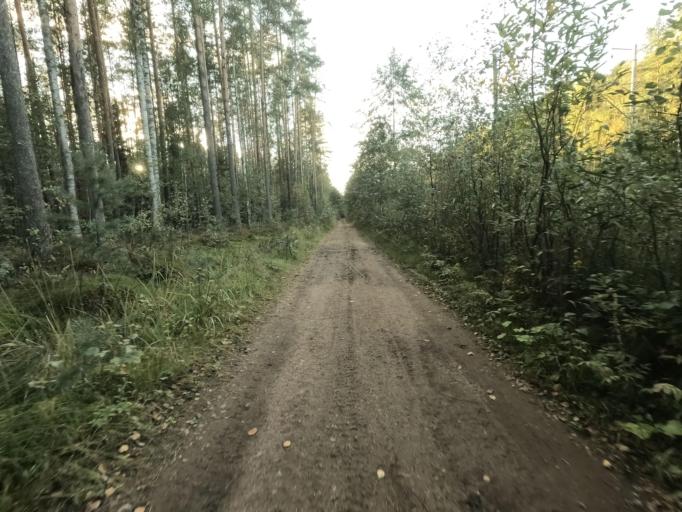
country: RU
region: Leningrad
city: Otradnoye
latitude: 59.8417
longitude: 30.7771
